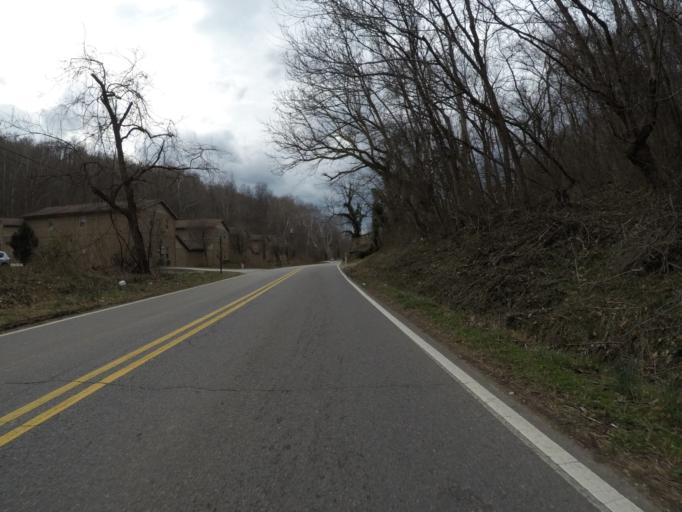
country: US
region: Ohio
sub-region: Lawrence County
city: Burlington
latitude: 38.4232
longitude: -82.5062
